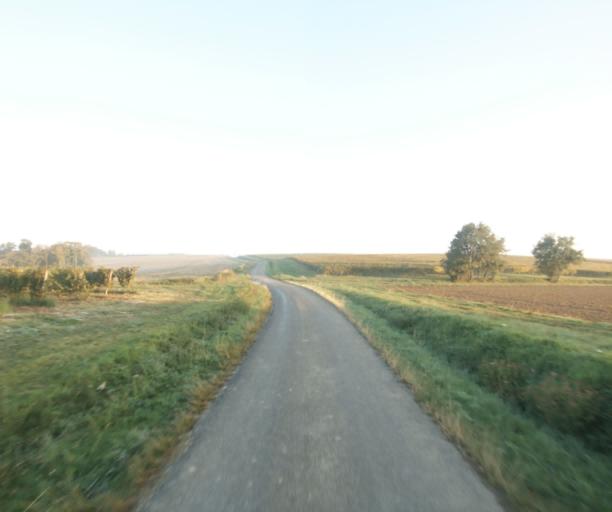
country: FR
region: Midi-Pyrenees
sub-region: Departement du Gers
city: Eauze
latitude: 43.7954
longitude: 0.1708
